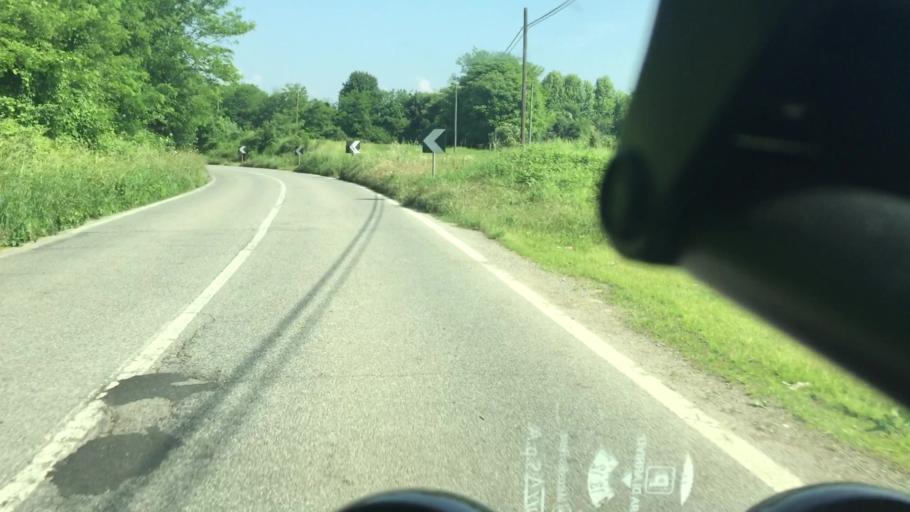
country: IT
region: Lombardy
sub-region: Provincia di Bergamo
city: Pontirolo Nuovo
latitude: 45.5538
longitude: 9.5663
